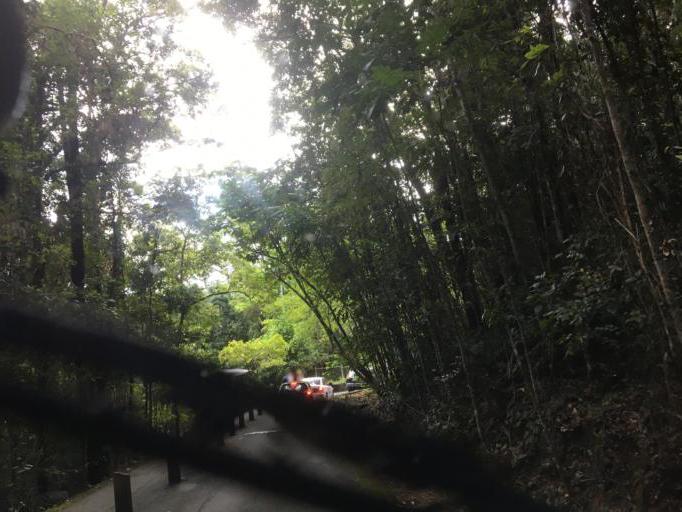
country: AU
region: Queensland
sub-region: Tablelands
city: Kuranda
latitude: -16.8362
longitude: 145.6417
